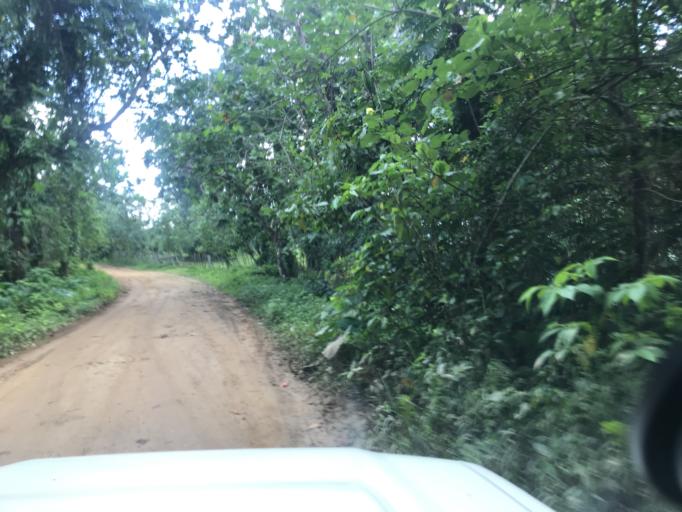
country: VU
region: Sanma
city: Luganville
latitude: -15.4894
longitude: 167.0899
